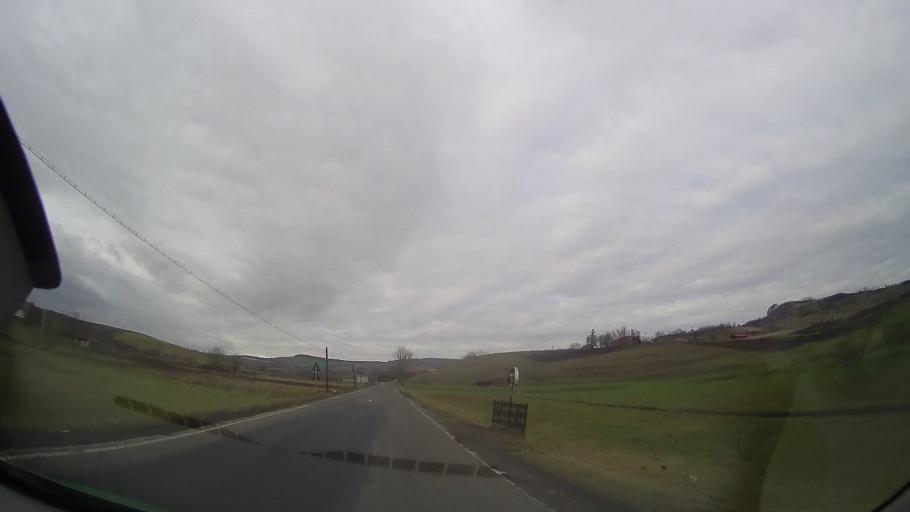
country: RO
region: Bistrita-Nasaud
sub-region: Comuna Urmenis
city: Urmenis
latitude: 46.7638
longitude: 24.3765
